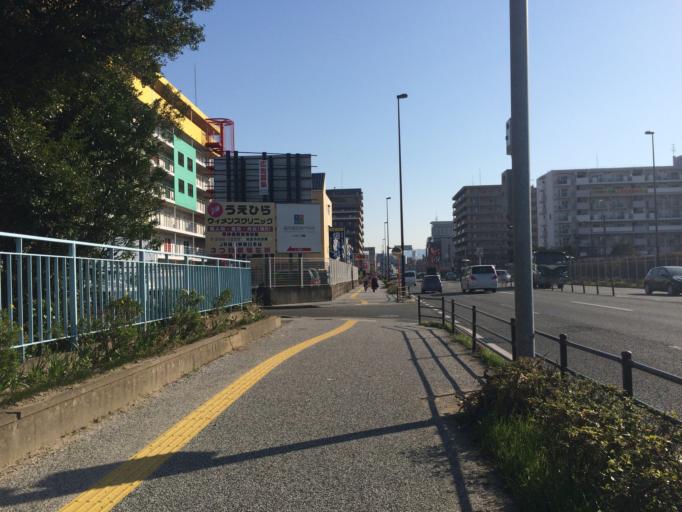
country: JP
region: Fukuoka
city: Fukuoka-shi
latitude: 33.6266
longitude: 130.4215
